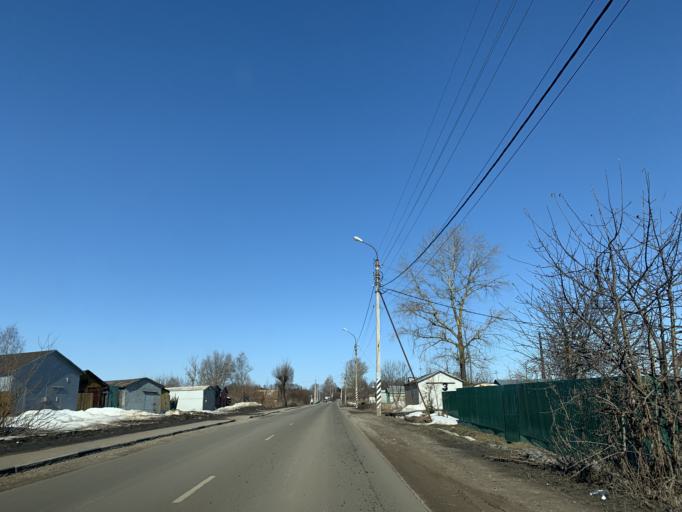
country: RU
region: Jaroslavl
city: Konstantinovskiy
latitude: 57.8343
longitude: 39.5888
